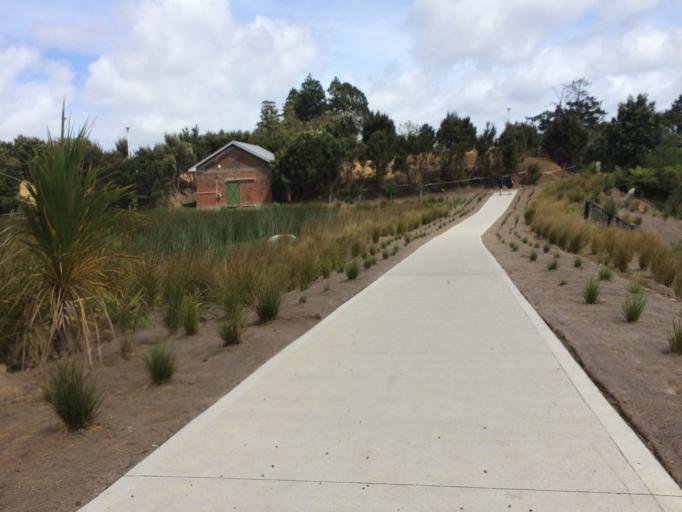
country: NZ
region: Auckland
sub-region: Auckland
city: North Shore
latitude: -36.7940
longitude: 174.6729
